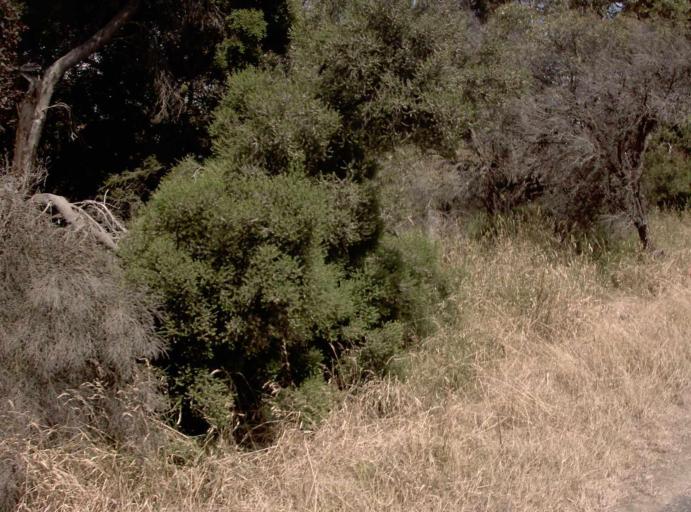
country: AU
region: Victoria
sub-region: Wellington
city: Heyfield
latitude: -38.0189
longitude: 146.8818
